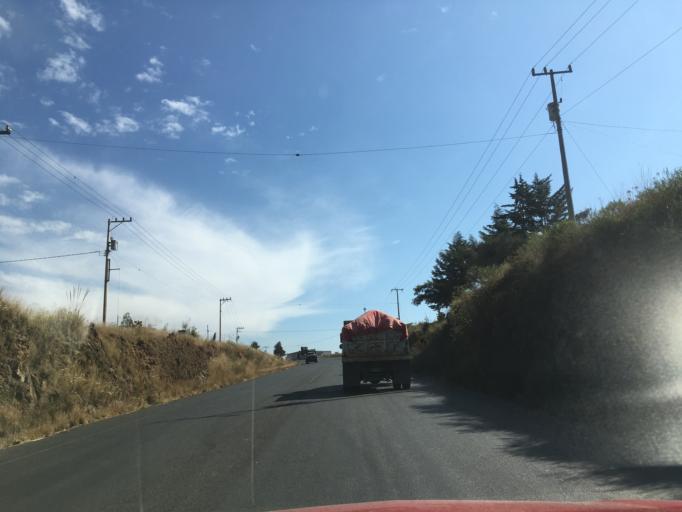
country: MX
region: Michoacan
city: Ciudad Hidalgo
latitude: 19.7028
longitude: -100.5749
